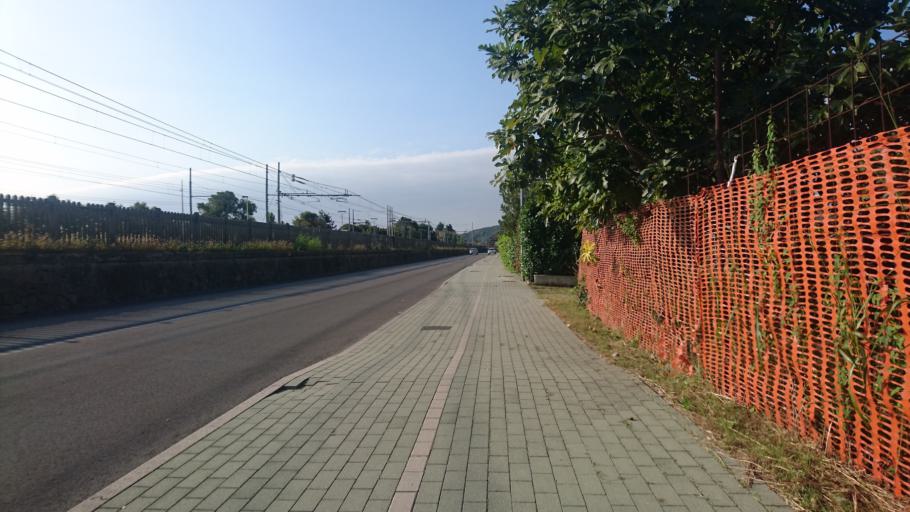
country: IT
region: Veneto
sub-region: Provincia di Padova
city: Montegrotto Terme
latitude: 45.3307
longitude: 11.7978
